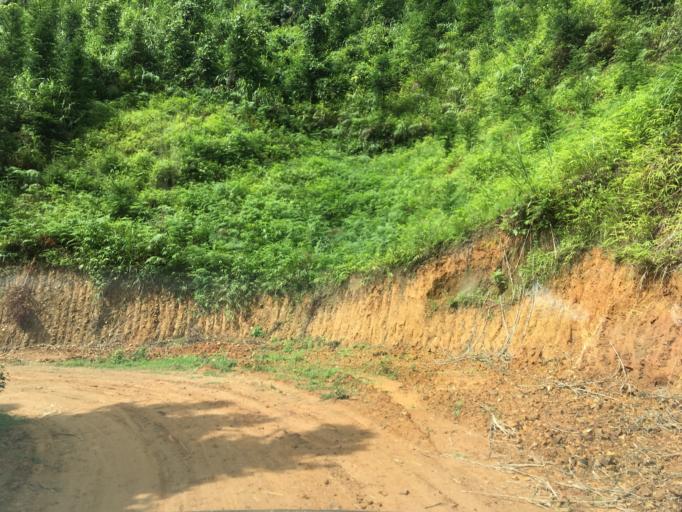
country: CN
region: Guangxi Zhuangzu Zizhiqu
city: Xinzhou
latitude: 24.8680
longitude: 105.8500
